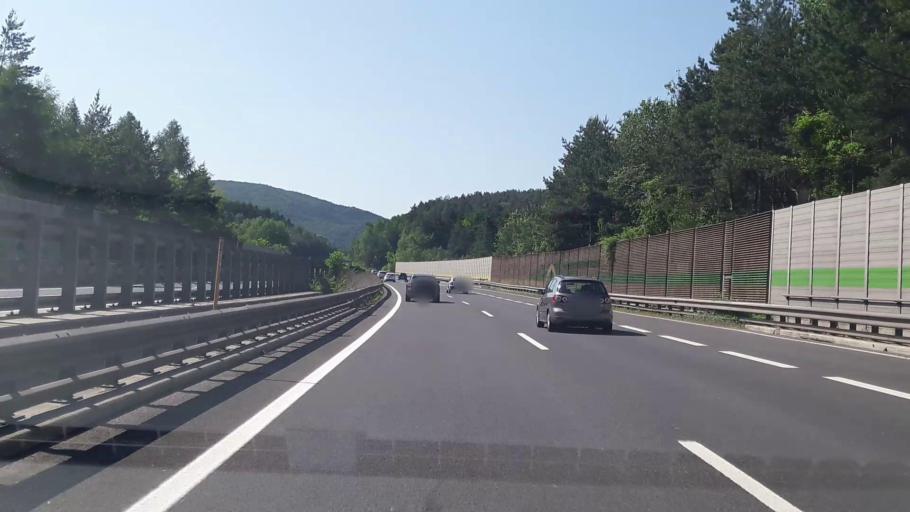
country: AT
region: Lower Austria
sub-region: Politischer Bezirk Neunkirchen
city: Seebenstein
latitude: 47.6775
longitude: 16.1237
